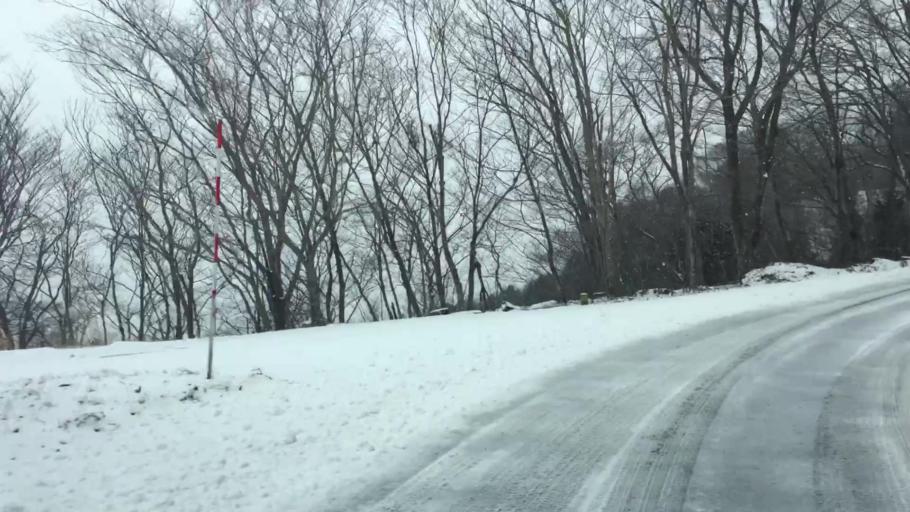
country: JP
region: Tochigi
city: Imaichi
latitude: 36.8852
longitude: 139.7318
